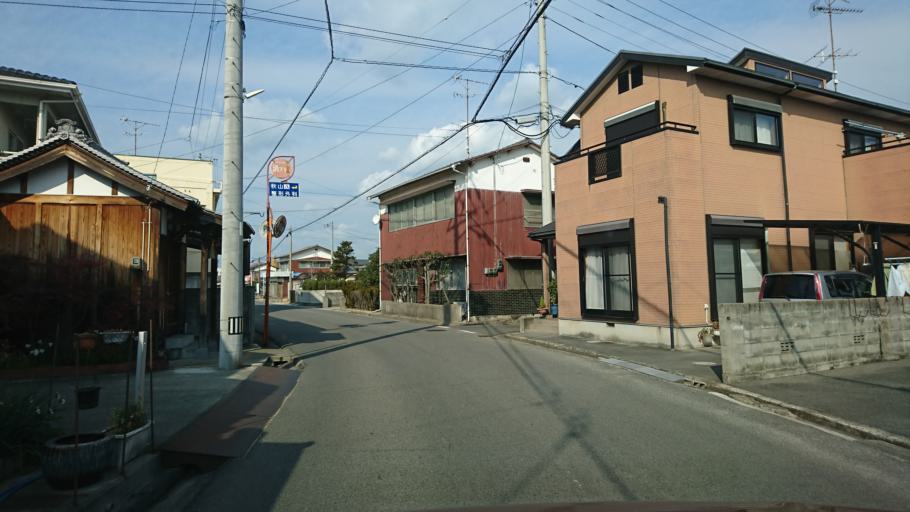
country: JP
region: Ehime
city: Saijo
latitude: 34.0230
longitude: 133.0392
